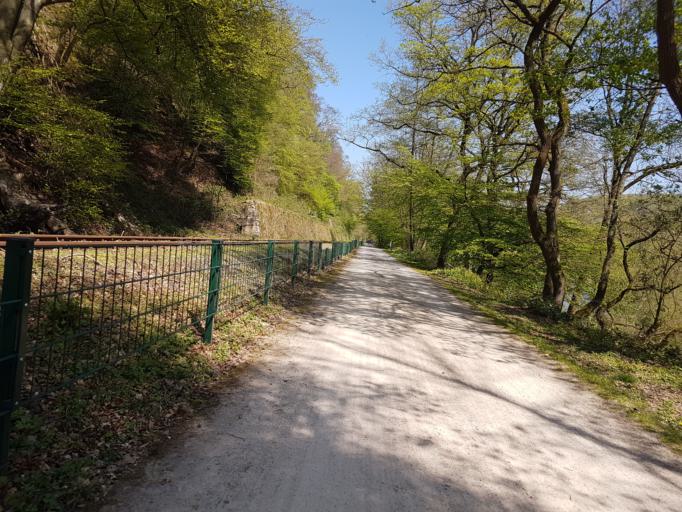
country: DE
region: North Rhine-Westphalia
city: Witten
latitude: 51.4145
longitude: 7.3462
